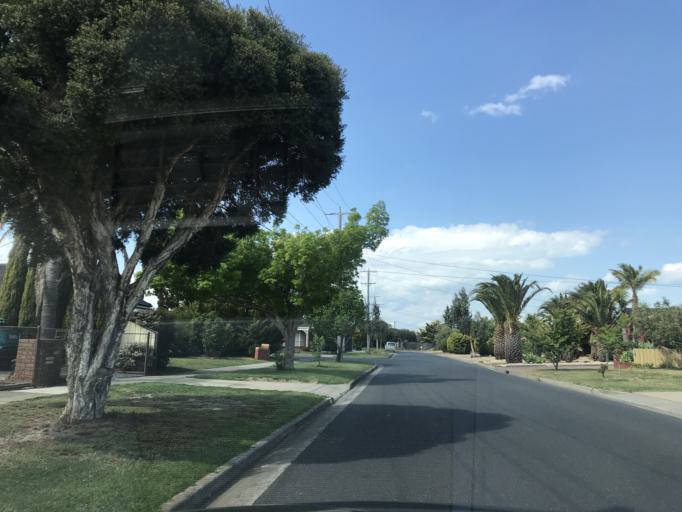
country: AU
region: Victoria
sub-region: Wyndham
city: Hoppers Crossing
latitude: -37.8644
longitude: 144.7124
